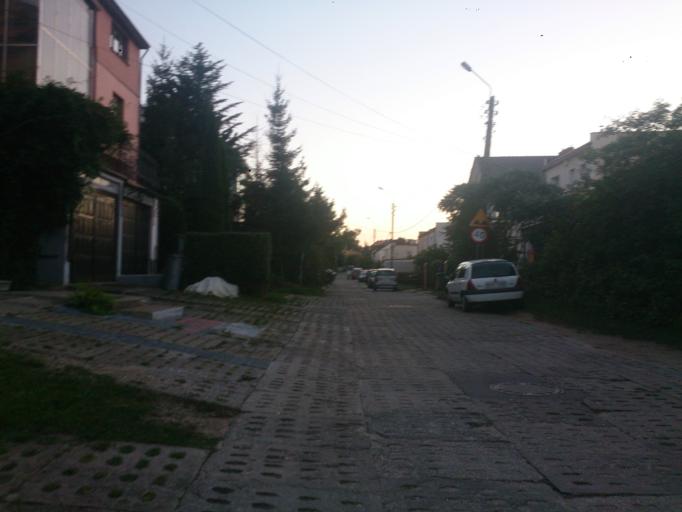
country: PL
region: Pomeranian Voivodeship
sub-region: Gdynia
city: Wielki Kack
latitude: 54.4772
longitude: 18.5239
